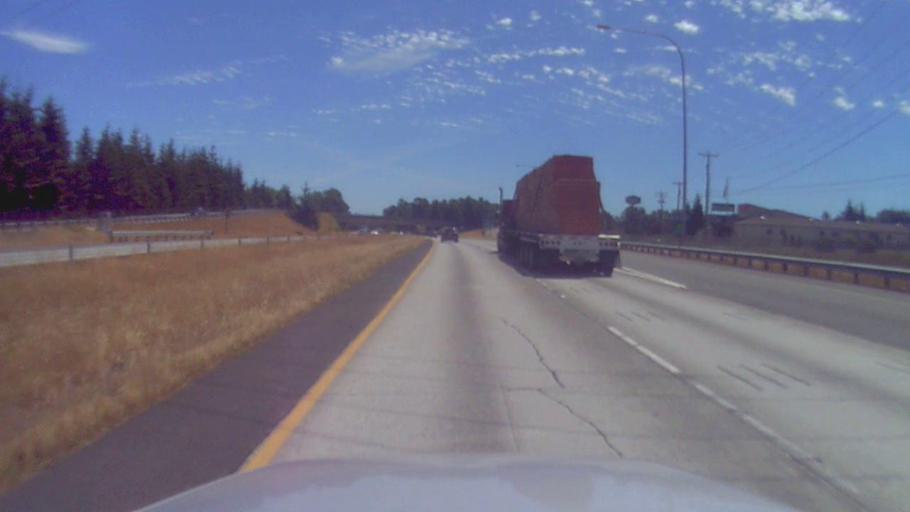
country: US
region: Washington
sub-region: Whatcom County
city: Marietta-Alderwood
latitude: 48.7908
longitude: -122.5214
